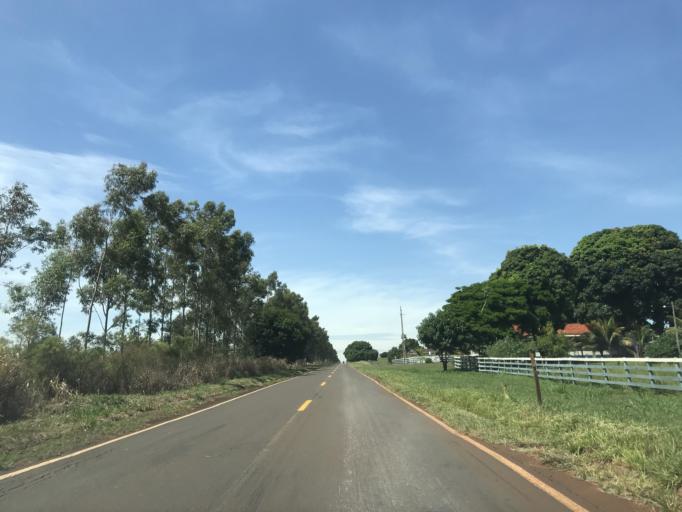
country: BR
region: Parana
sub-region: Paranavai
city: Nova Aurora
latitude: -22.8230
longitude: -52.6553
